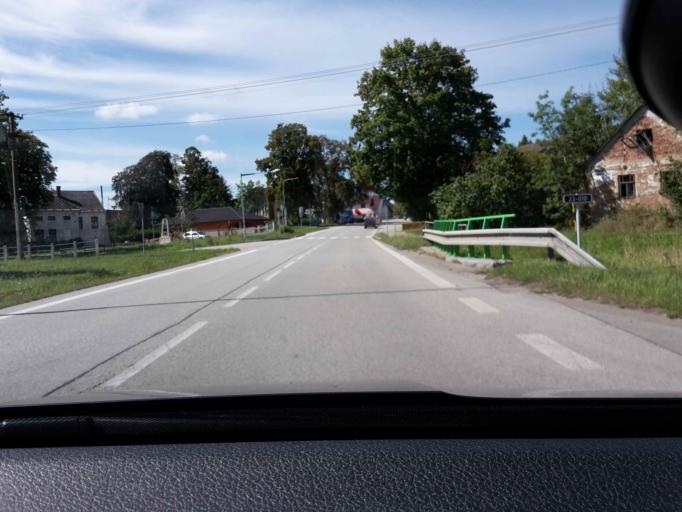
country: CZ
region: Jihocesky
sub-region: Okres Jindrichuv Hradec
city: Jindrichuv Hradec
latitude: 49.1592
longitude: 14.9575
